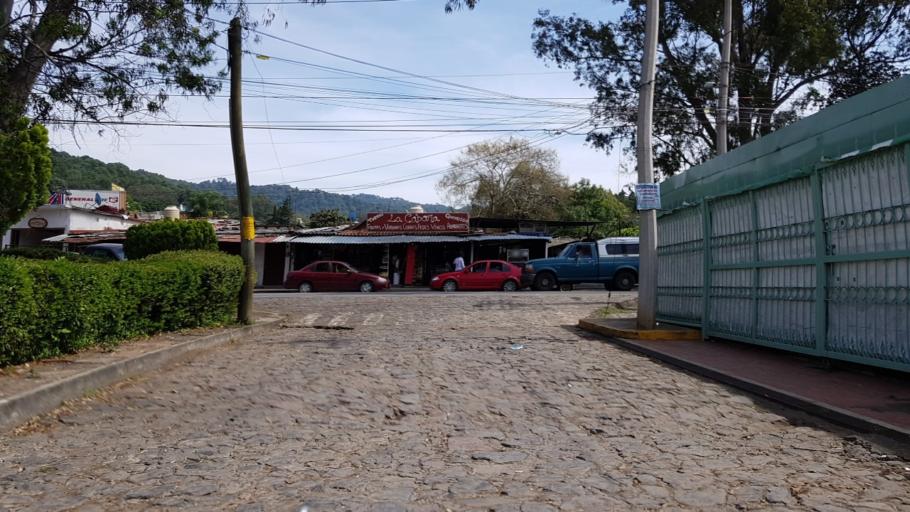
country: MX
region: Mexico
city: Valle de Bravo
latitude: 19.2053
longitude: -100.1341
